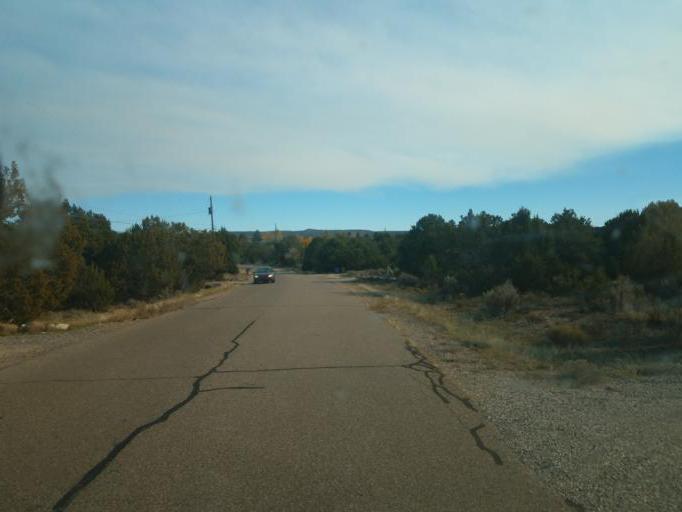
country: US
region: New Mexico
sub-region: Los Alamos County
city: White Rock
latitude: 35.8114
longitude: -106.2204
